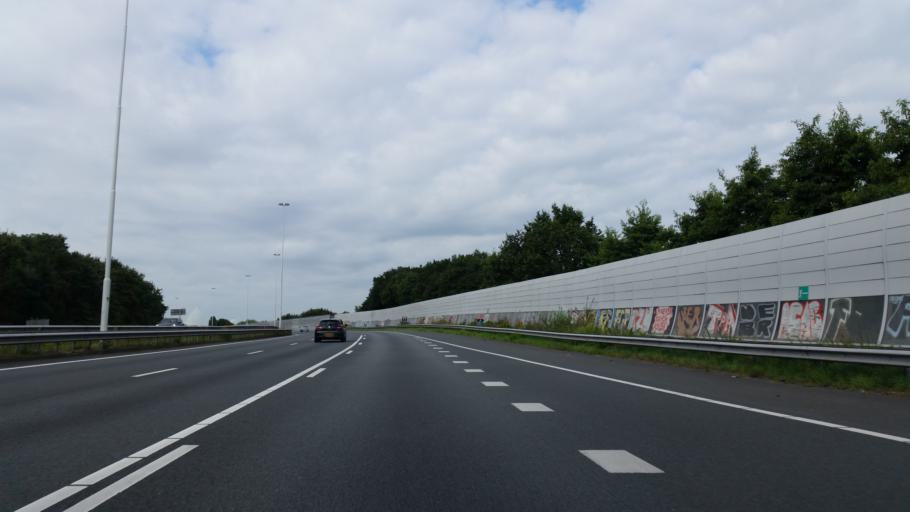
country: NL
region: South Holland
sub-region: Gemeente Rotterdam
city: Rotterdam
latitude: 51.9453
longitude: 4.4974
